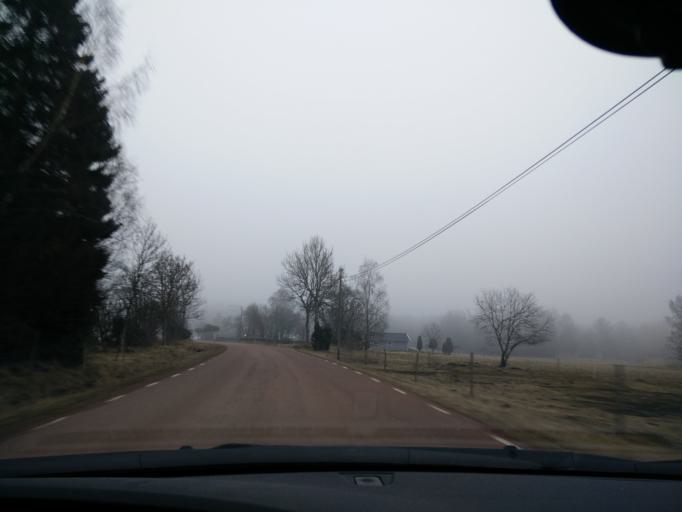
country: AX
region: Mariehamns stad
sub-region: Mariehamn
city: Mariehamn
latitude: 60.1036
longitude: 19.9007
